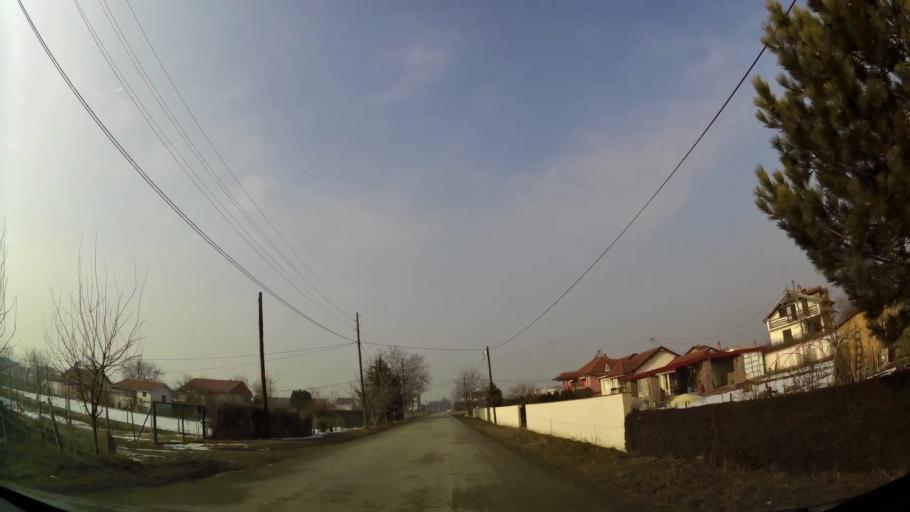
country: MK
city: Kadino
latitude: 41.9801
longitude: 21.5977
